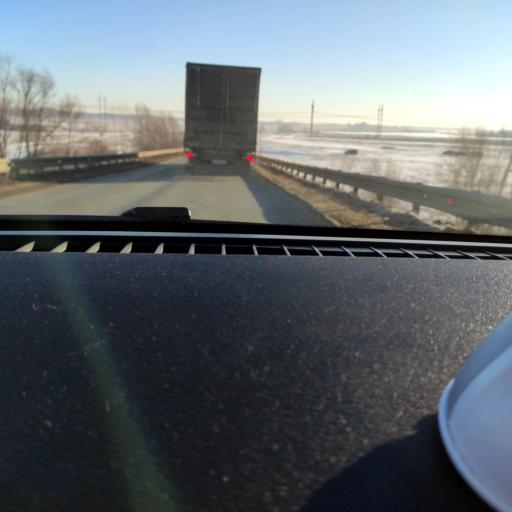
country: RU
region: Samara
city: Spiridonovka
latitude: 53.1433
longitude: 50.5891
